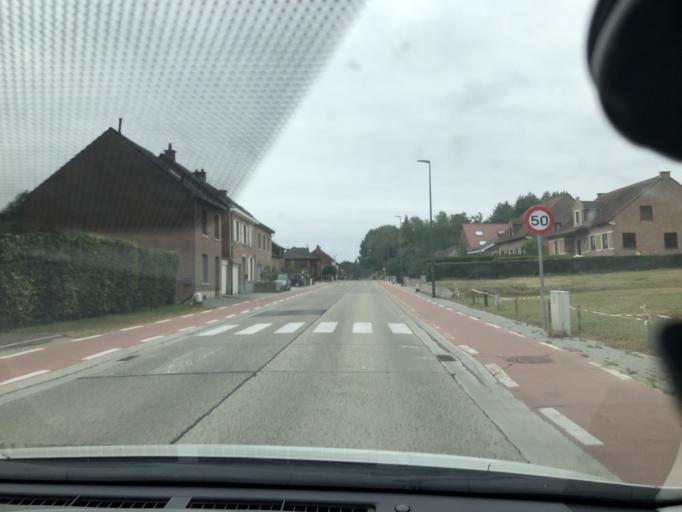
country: BE
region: Flanders
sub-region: Provincie Vlaams-Brabant
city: Oud-Heverlee
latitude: 50.8421
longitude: 4.6697
